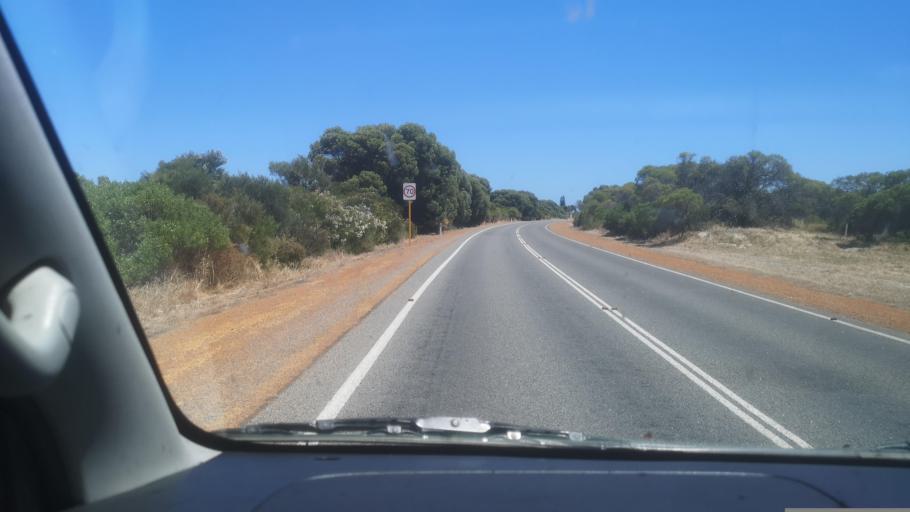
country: AU
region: Western Australia
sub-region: Dandaragan
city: Jurien Bay
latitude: -30.3196
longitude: 115.0383
